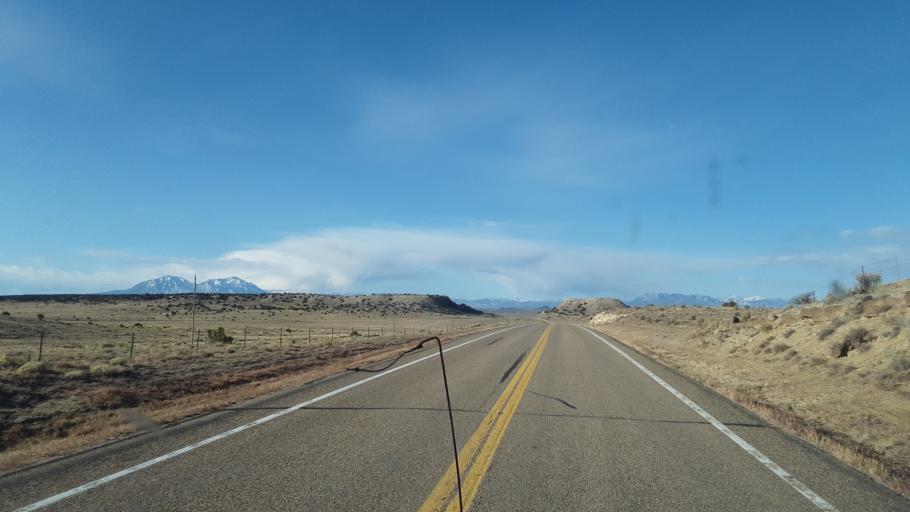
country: US
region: Colorado
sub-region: Huerfano County
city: Walsenburg
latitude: 37.6979
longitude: -104.6157
